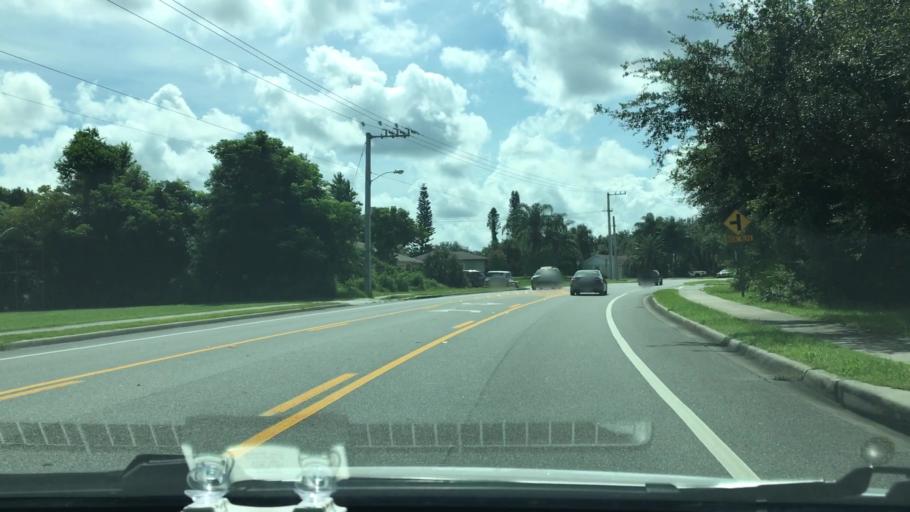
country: US
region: Florida
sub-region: Volusia County
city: Deltona
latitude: 28.8891
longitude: -81.2117
